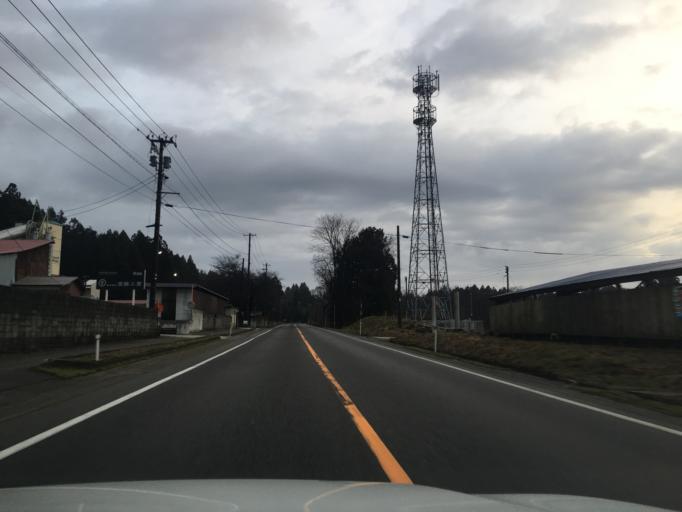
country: JP
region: Niigata
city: Murakami
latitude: 38.2909
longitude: 139.5275
